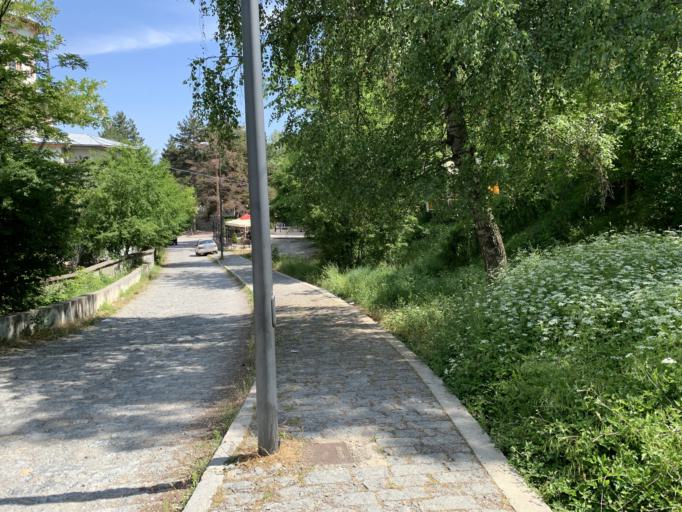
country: AL
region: Korce
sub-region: Rrethi i Korces
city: Korce
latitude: 40.6245
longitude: 20.7842
